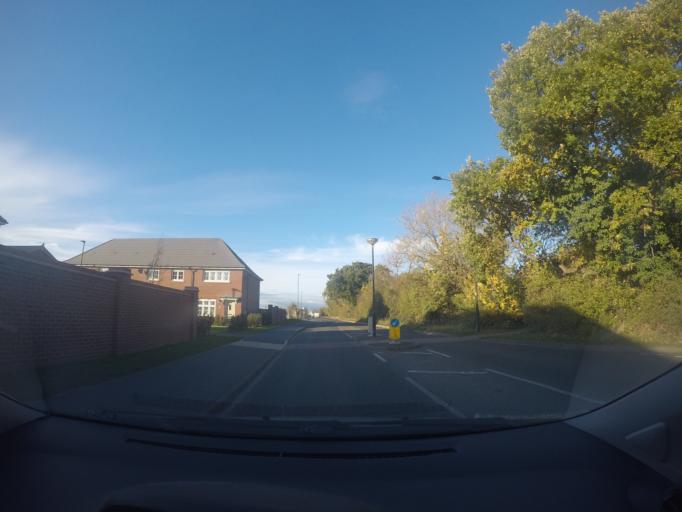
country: GB
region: England
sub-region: City of York
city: York
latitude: 53.9828
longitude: -1.0941
